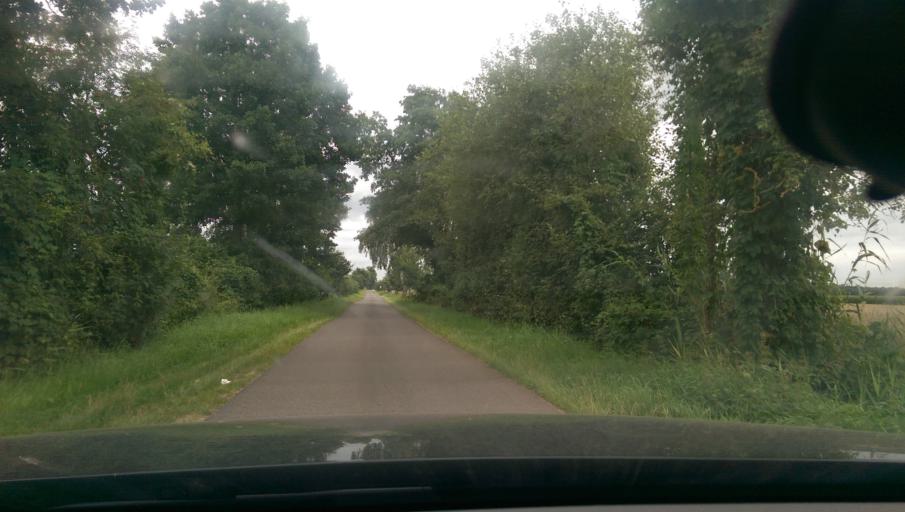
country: DE
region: Lower Saxony
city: Wietze
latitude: 52.5988
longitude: 9.8051
